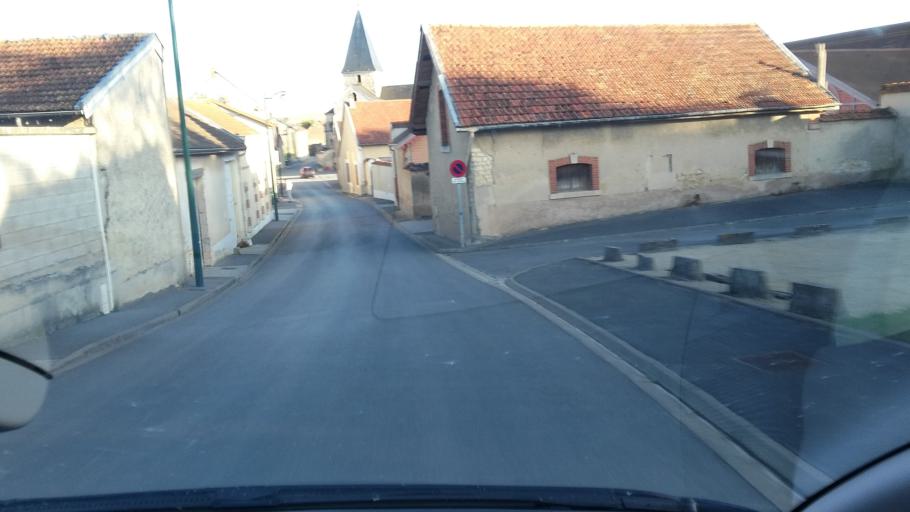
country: FR
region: Champagne-Ardenne
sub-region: Departement de la Marne
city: Cormontreuil
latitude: 49.1930
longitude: 4.0402
